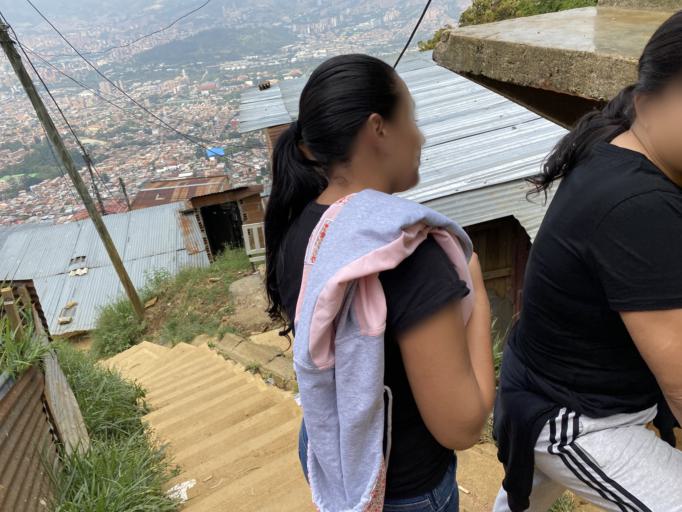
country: CO
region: Antioquia
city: Medellin
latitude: 6.2646
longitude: -75.5404
